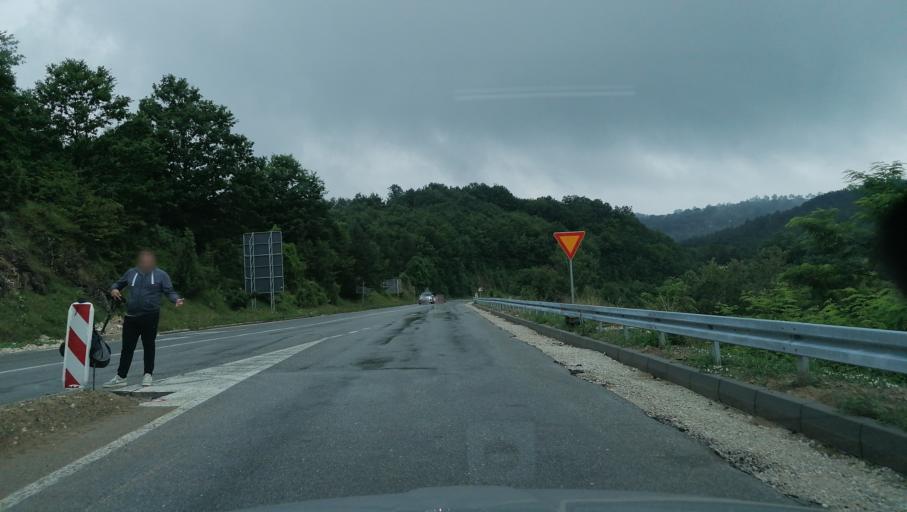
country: RS
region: Central Serbia
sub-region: Zlatiborski Okrug
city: Cajetina
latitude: 43.7840
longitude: 19.7372
